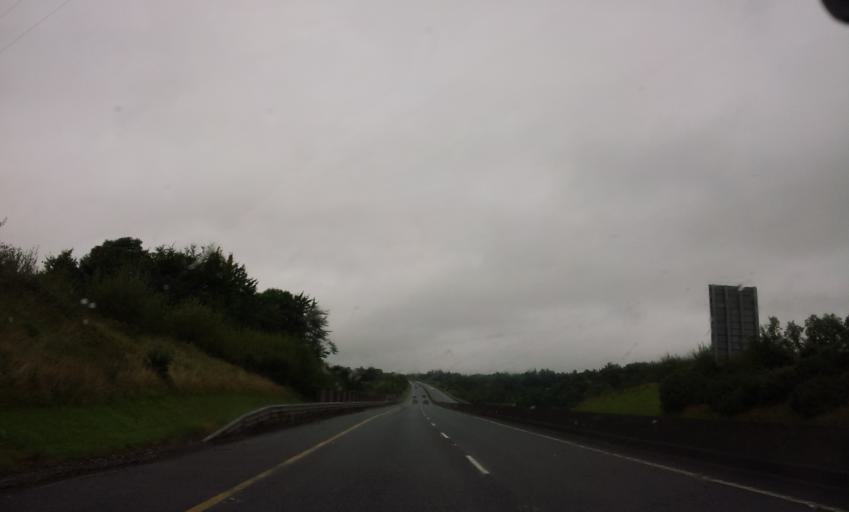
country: IE
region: Munster
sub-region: County Cork
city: Fermoy
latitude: 52.1783
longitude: -8.2718
